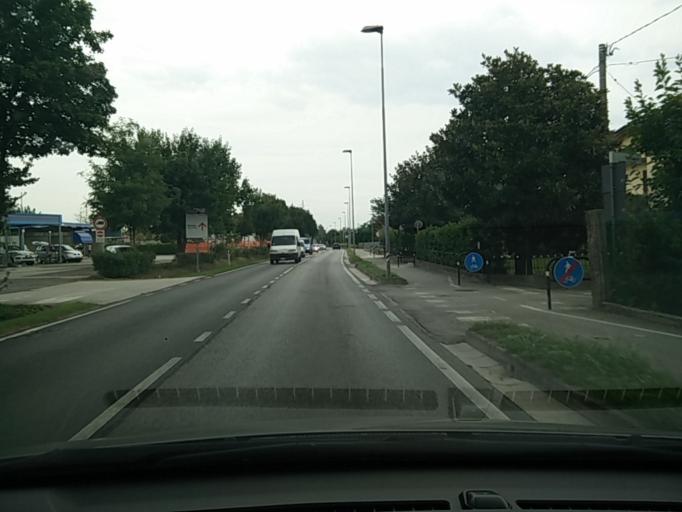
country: IT
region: Veneto
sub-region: Provincia di Treviso
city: Padernello
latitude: 45.6766
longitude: 12.1405
